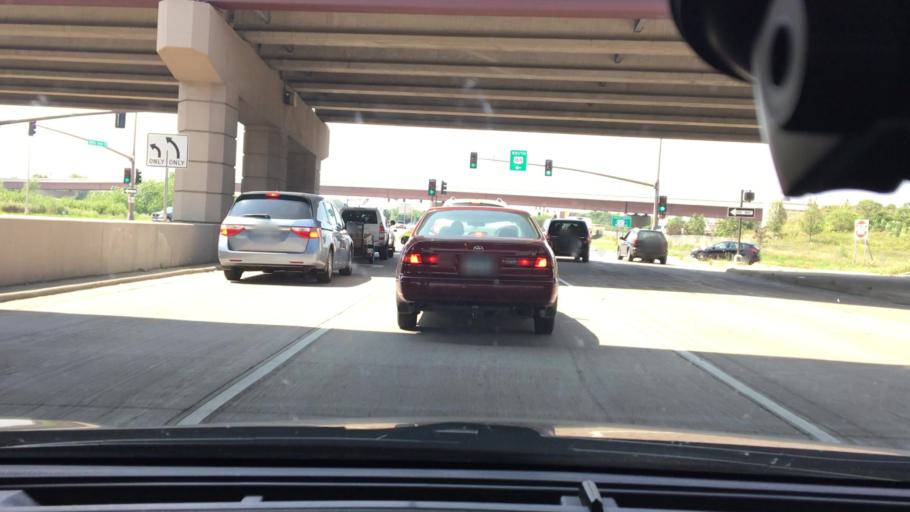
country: US
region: Minnesota
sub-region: Hennepin County
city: Osseo
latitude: 45.1090
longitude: -93.3915
